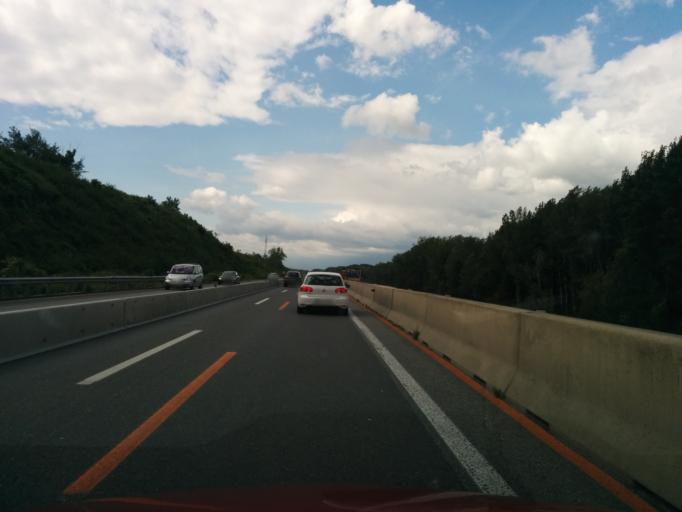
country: AT
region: Lower Austria
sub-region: Politischer Bezirk Wien-Umgebung
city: Fischamend Dorf
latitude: 48.1249
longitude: 16.5997
